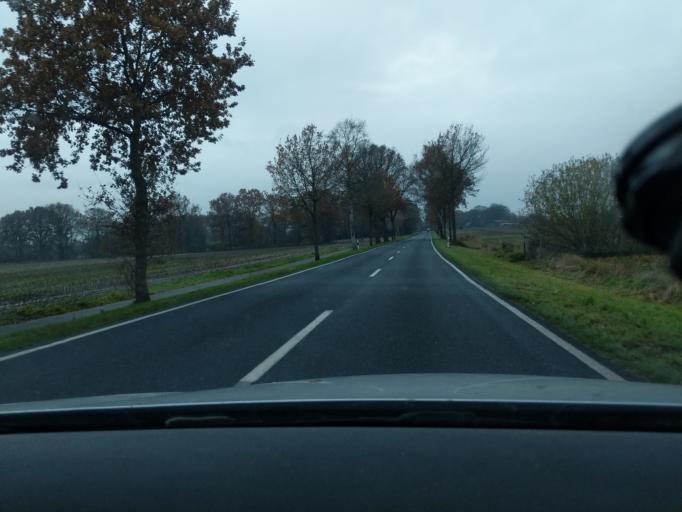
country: DE
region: Lower Saxony
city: Heeslingen
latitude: 53.3402
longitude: 9.3838
